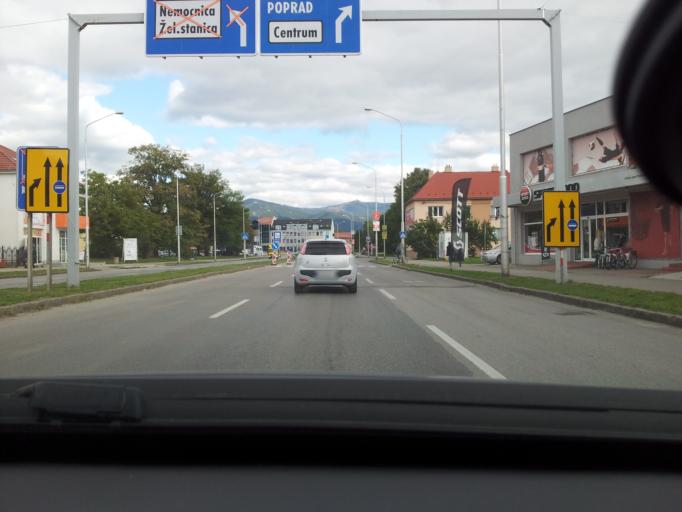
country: SK
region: Zilinsky
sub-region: Okres Martin
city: Martin
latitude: 49.0593
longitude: 18.9210
